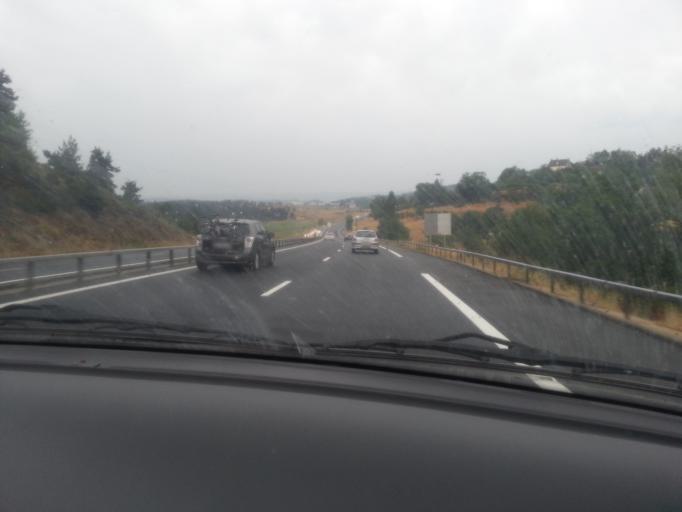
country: FR
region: Languedoc-Roussillon
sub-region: Departement de la Lozere
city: Aumont-Aubrac
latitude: 44.7226
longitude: 3.2784
